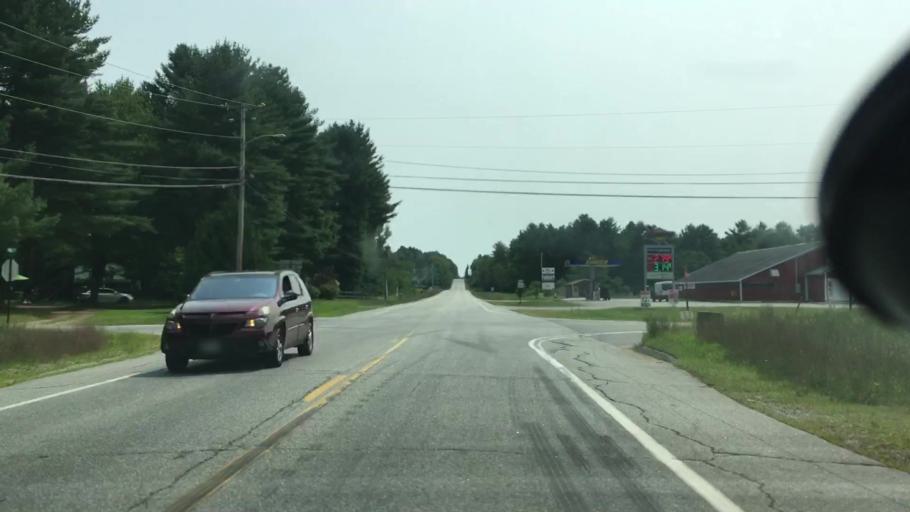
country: US
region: Maine
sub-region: Kennebec County
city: Wayne
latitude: 44.4038
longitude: -70.1301
